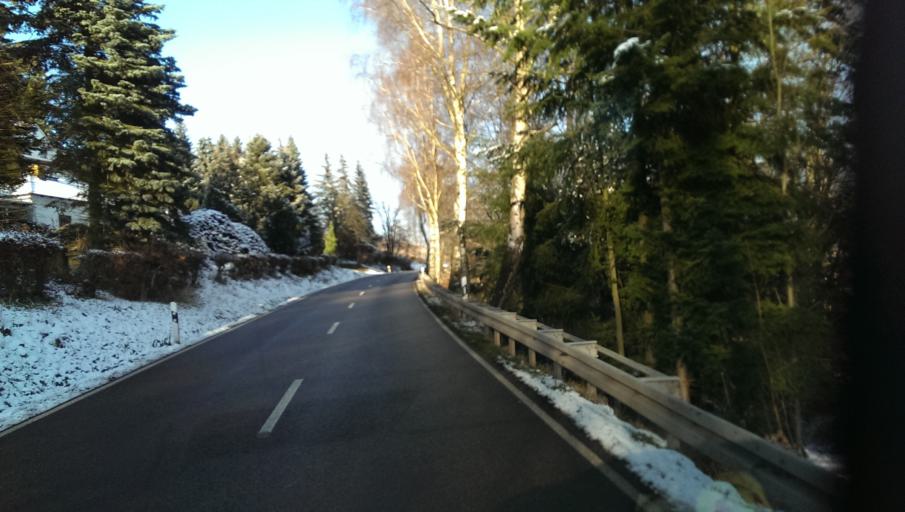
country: DE
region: Saxony
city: Dippoldiswalde
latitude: 50.8925
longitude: 13.6598
